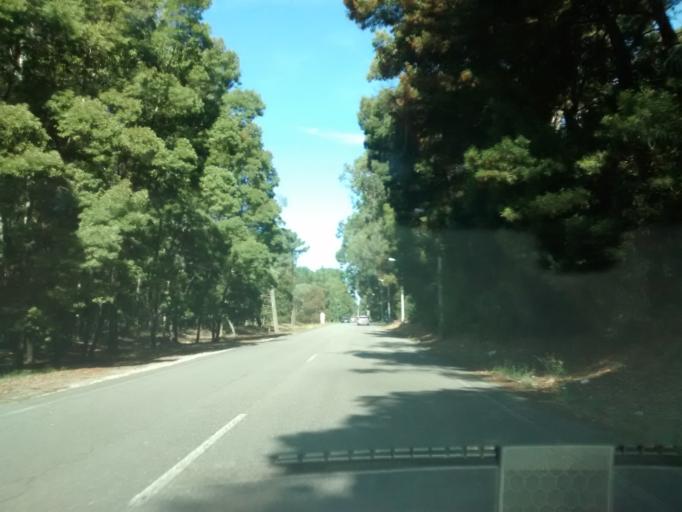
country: PT
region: Coimbra
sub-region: Mira
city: Mira
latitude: 40.4509
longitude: -8.7708
